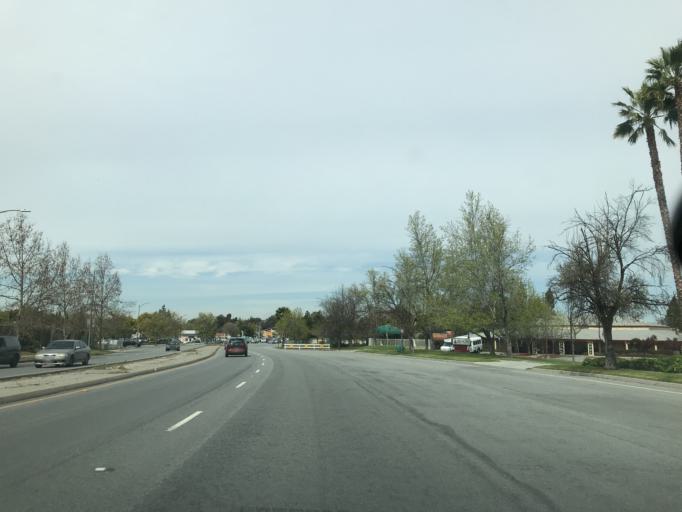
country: US
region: California
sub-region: Santa Clara County
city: Seven Trees
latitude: 37.3125
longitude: -121.7888
